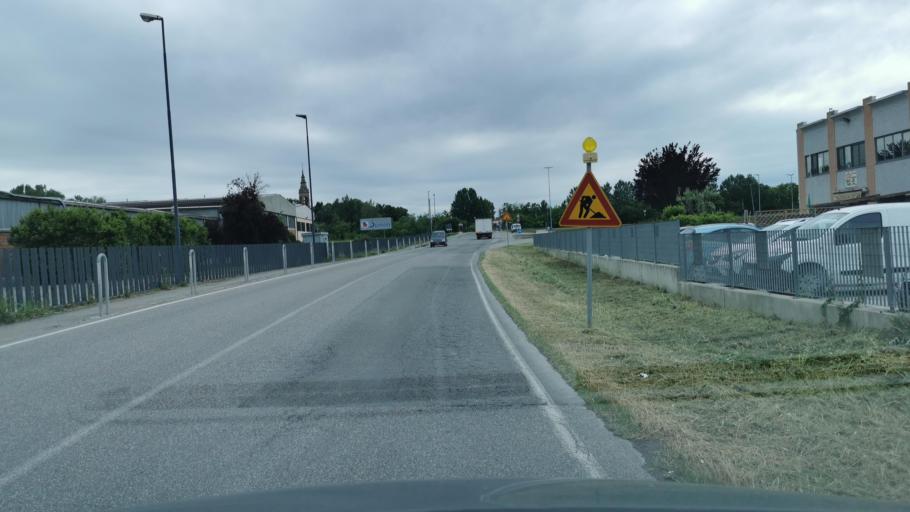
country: IT
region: Emilia-Romagna
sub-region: Provincia di Parma
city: Soragna
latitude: 44.9182
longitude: 10.1120
